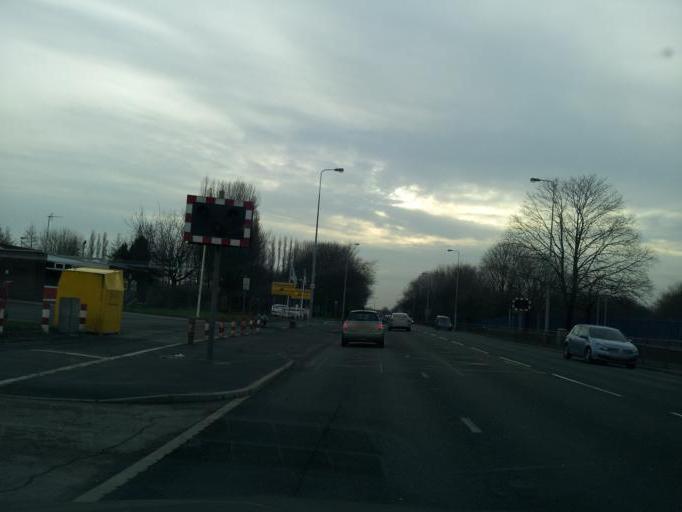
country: GB
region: England
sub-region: Borough of Oldham
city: Royton
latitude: 53.5491
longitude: -2.1440
